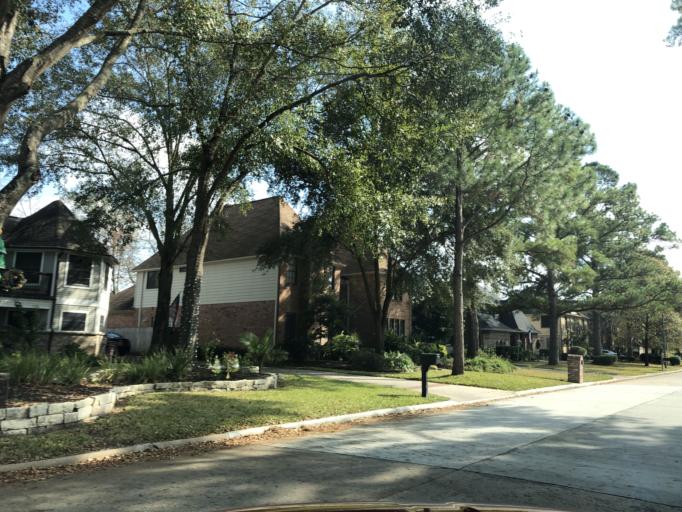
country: US
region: Texas
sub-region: Harris County
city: Tomball
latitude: 30.0312
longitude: -95.5459
